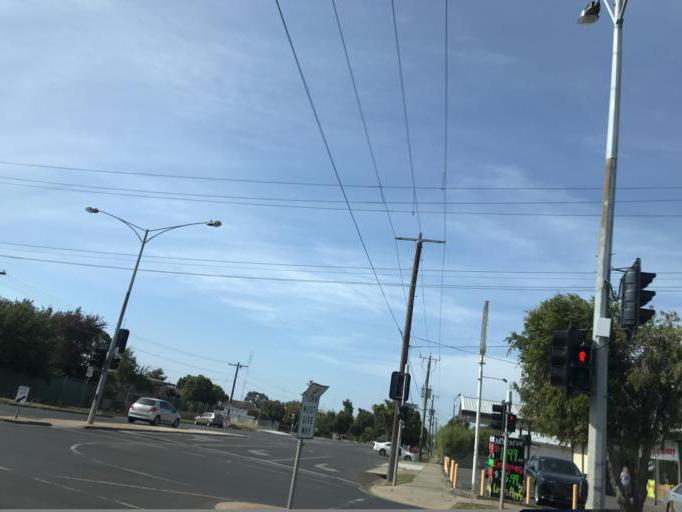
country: AU
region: Victoria
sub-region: Ballarat North
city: Lake Wendouree
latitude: -37.5414
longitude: 143.8405
